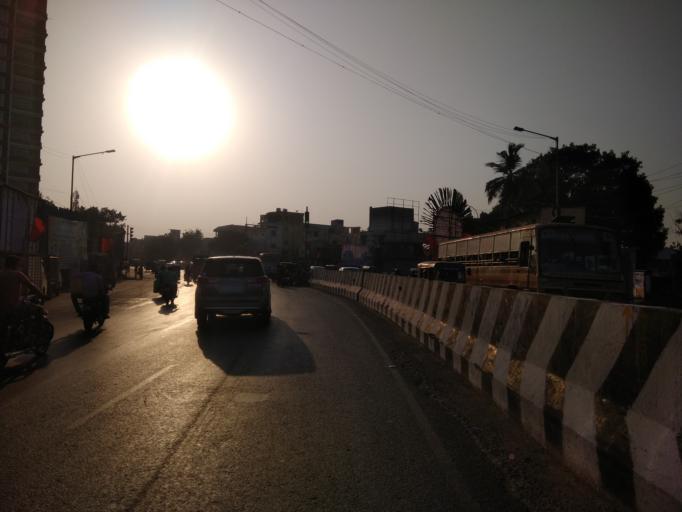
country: IN
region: Tamil Nadu
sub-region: Chennai
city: Chetput
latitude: 13.0767
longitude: 80.2122
